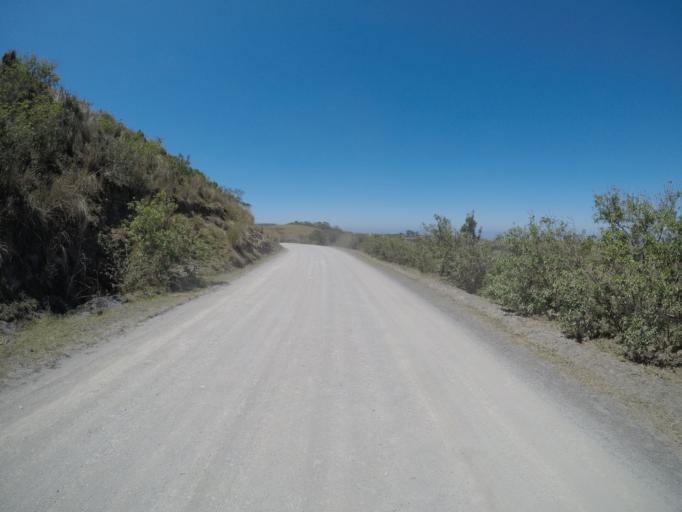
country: ZA
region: Eastern Cape
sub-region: OR Tambo District Municipality
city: Libode
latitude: -31.9975
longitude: 29.0607
